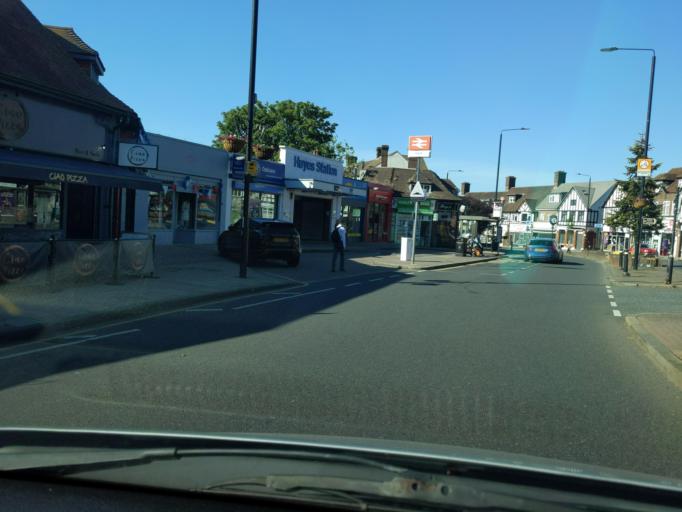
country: GB
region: England
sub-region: Greater London
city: West Wickham
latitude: 51.3760
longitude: 0.0107
